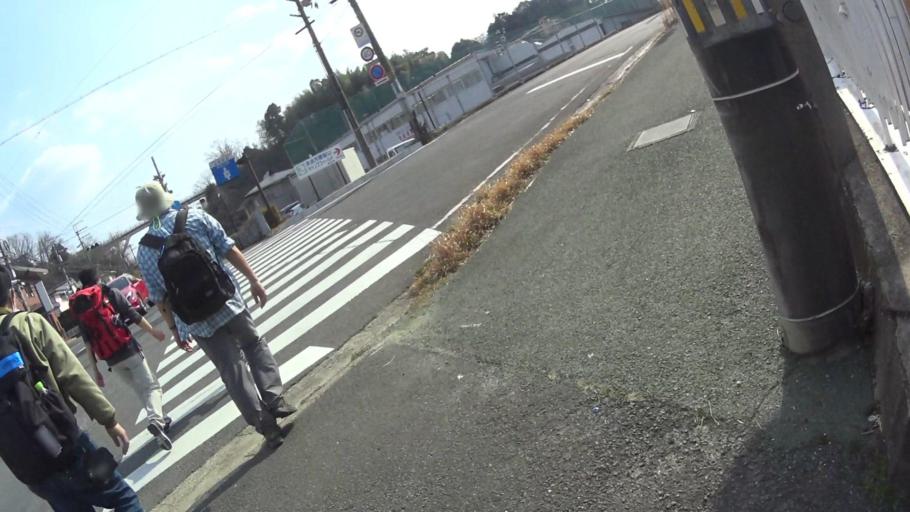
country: JP
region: Nara
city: Nara-shi
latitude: 34.7036
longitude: 135.8270
